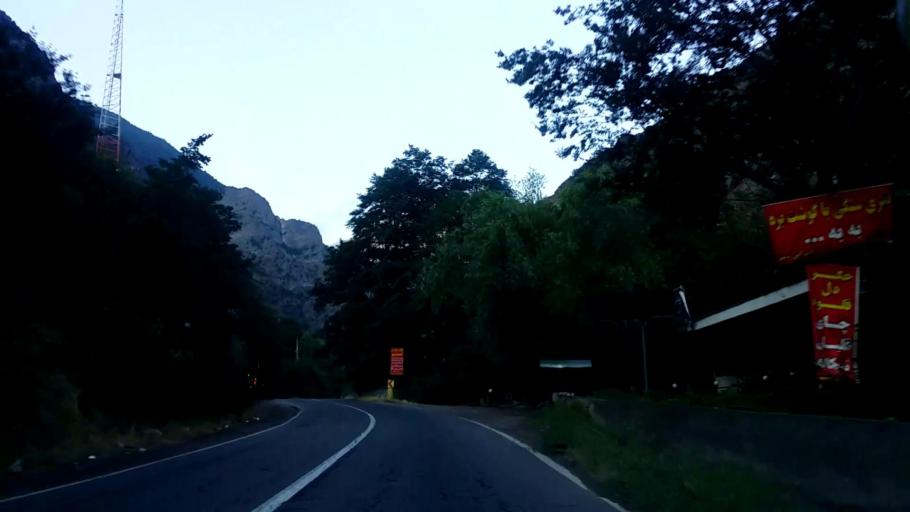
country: IR
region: Mazandaran
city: Chalus
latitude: 36.3294
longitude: 51.2551
